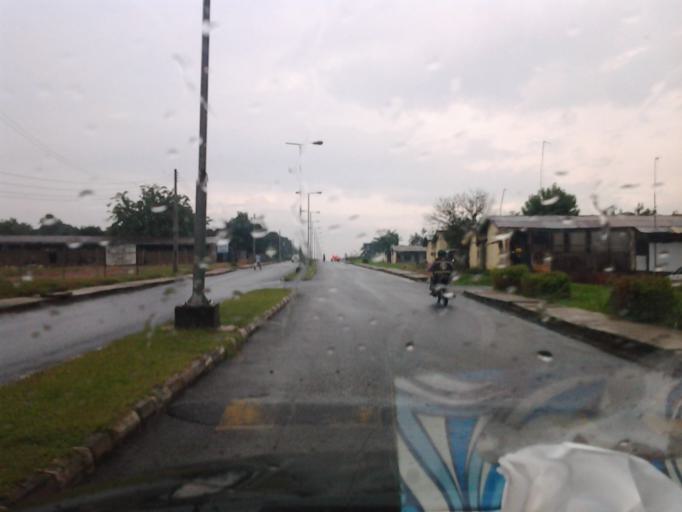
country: NG
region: Oyo
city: Moniya
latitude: 7.4554
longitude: 3.8989
